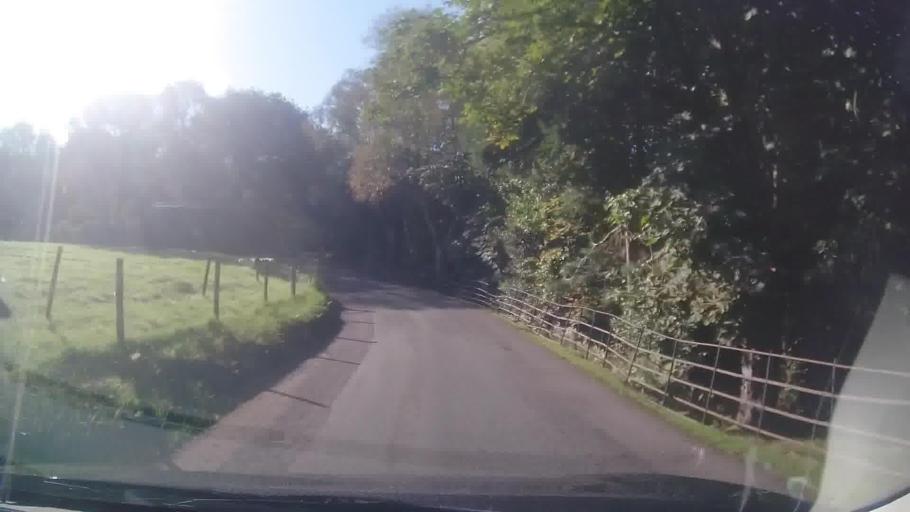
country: GB
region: England
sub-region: Cumbria
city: Seascale
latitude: 54.3962
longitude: -3.3791
